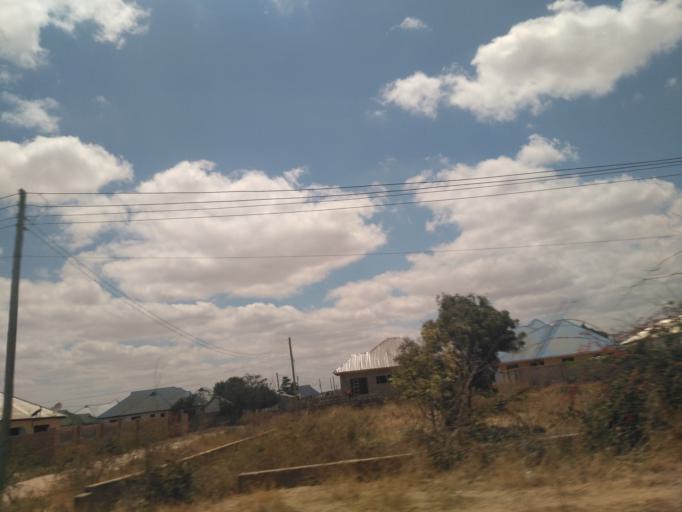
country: TZ
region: Dodoma
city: Kisasa
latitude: -6.1734
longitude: 35.7995
